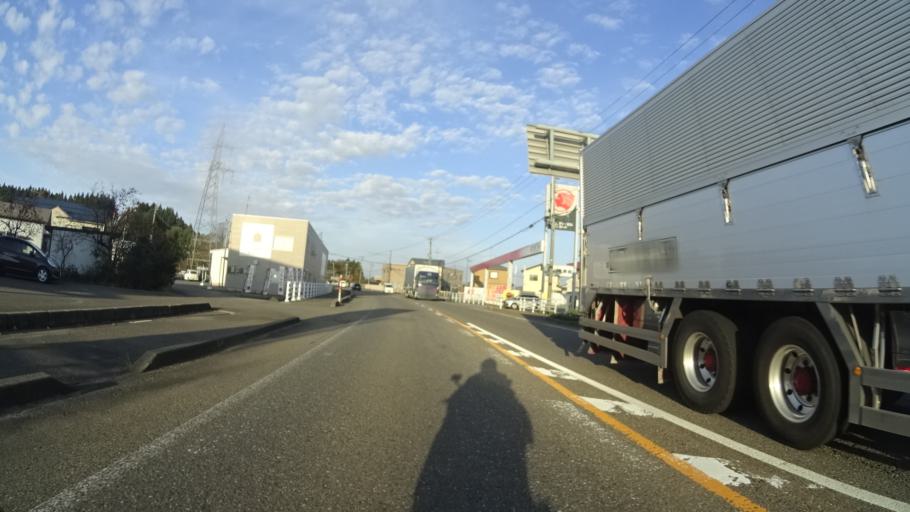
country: JP
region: Niigata
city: Kashiwazaki
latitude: 37.3931
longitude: 138.6013
